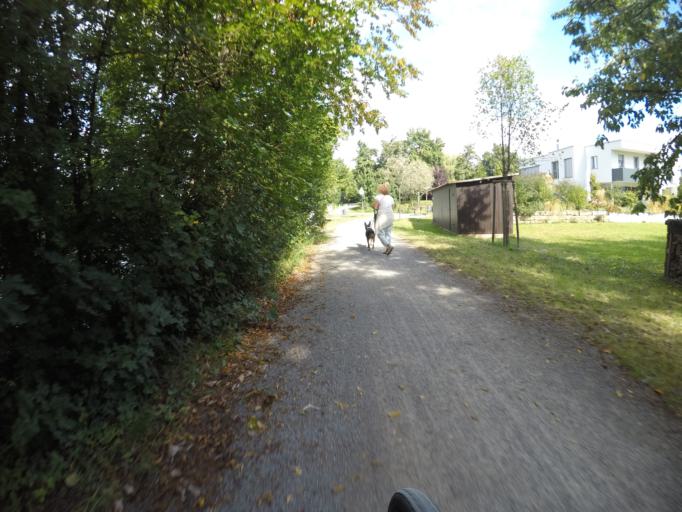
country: DE
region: Baden-Wuerttemberg
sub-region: Regierungsbezirk Stuttgart
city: Mundelsheim
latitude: 48.9960
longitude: 9.2036
